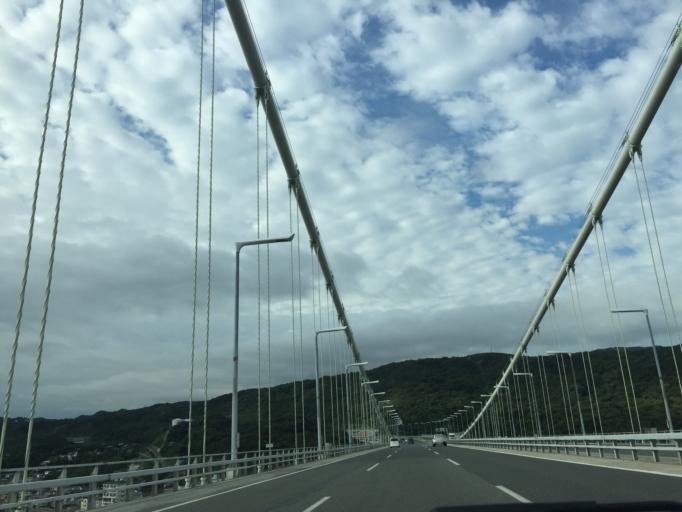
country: JP
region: Hyogo
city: Akashi
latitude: 34.6052
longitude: 135.0111
